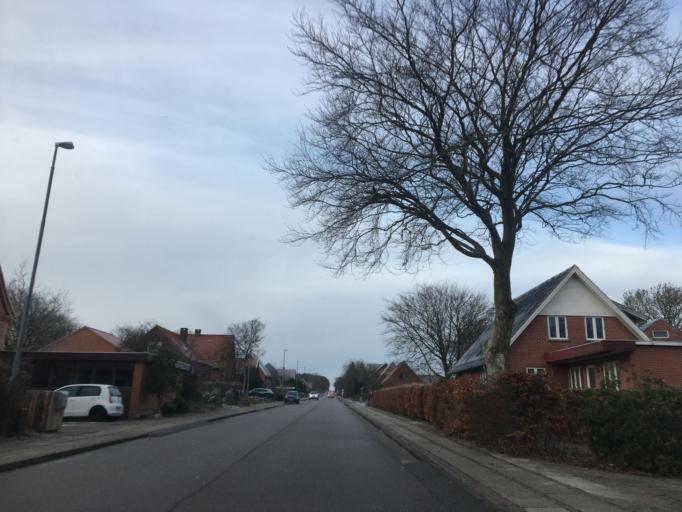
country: DK
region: North Denmark
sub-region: Thisted Kommune
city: Hurup
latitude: 56.7510
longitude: 8.4113
